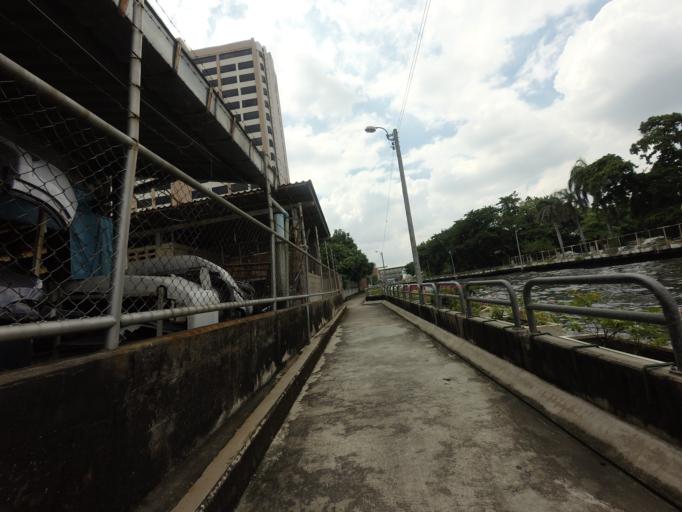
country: TH
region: Bangkok
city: Bang Kapi
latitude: 13.7639
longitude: 100.6392
